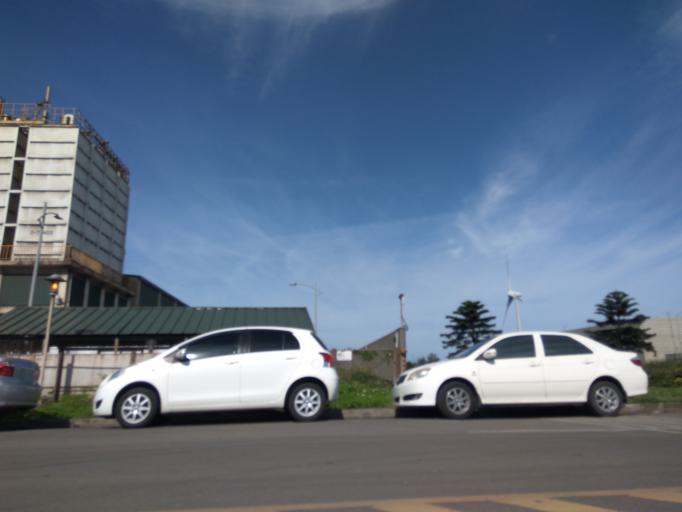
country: TW
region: Taiwan
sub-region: Hsinchu
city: Zhubei
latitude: 25.0348
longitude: 121.0568
